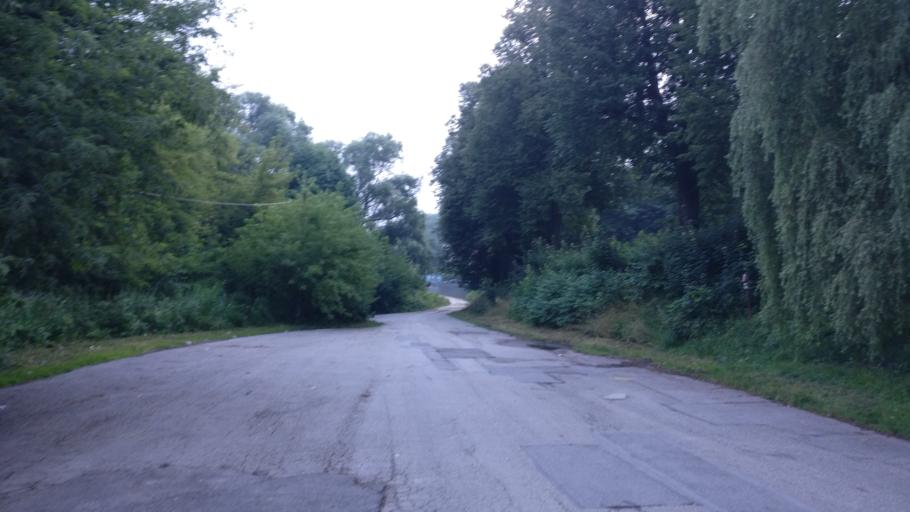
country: SK
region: Zilinsky
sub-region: Okres Zilina
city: Zilina
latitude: 49.2426
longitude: 18.7435
